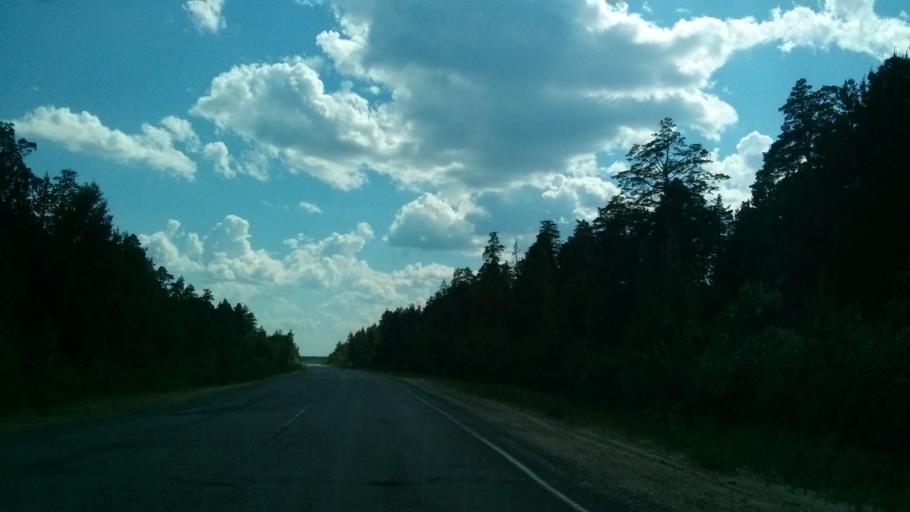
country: RU
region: Vladimir
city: Melenki
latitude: 55.3502
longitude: 41.6757
